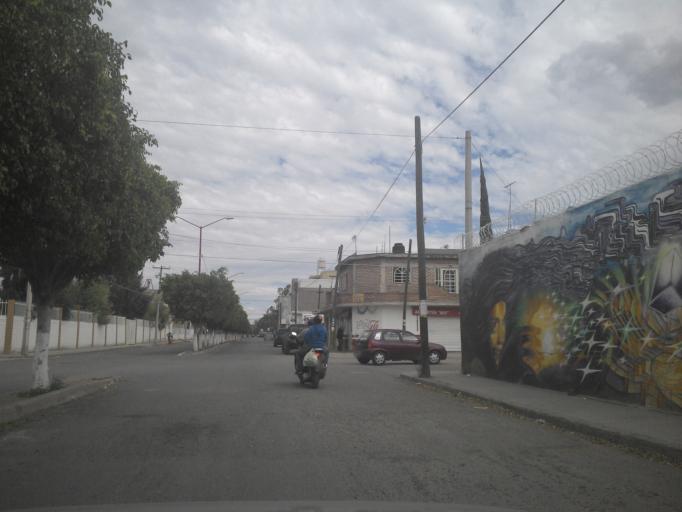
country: MX
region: Guanajuato
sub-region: San Francisco del Rincon
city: Fraccionamiento la Mezquitera
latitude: 21.0106
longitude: -101.8462
